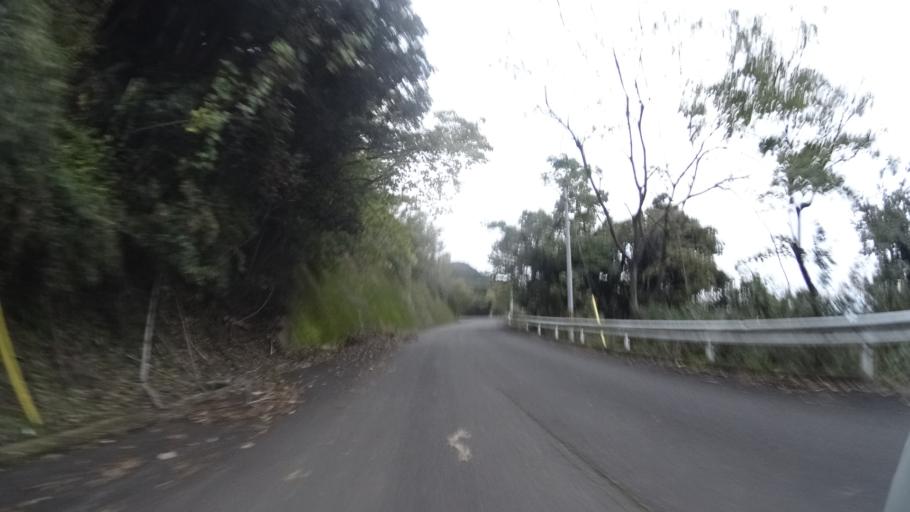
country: JP
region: Kyoto
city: Maizuru
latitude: 35.5659
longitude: 135.4627
